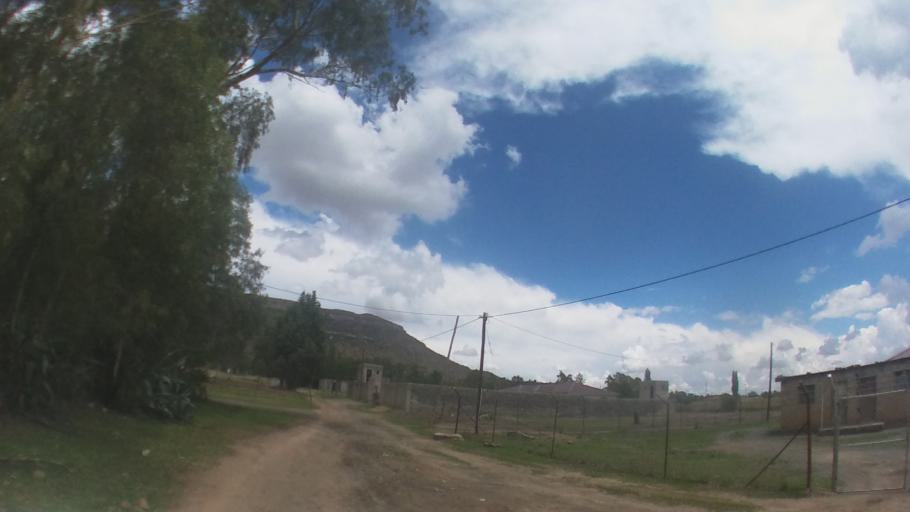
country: LS
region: Maseru
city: Nako
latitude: -29.6207
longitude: 27.5052
